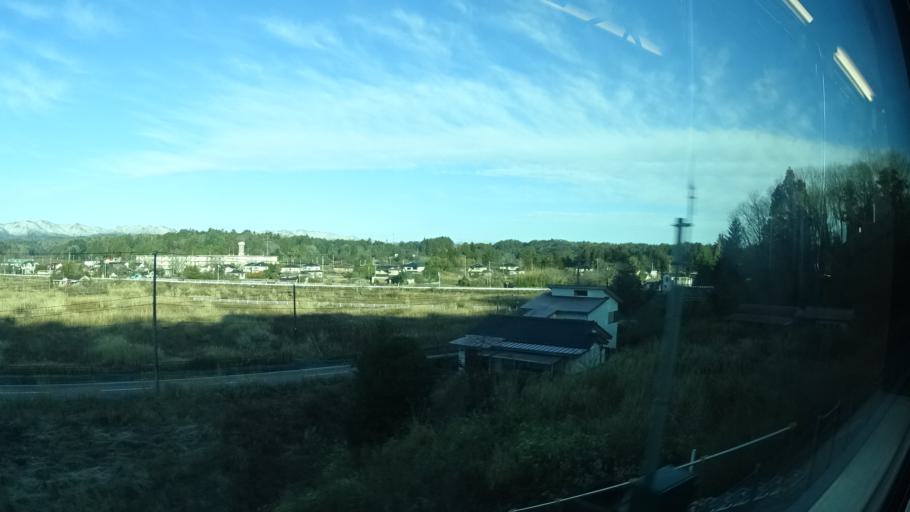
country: JP
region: Fukushima
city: Namie
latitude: 37.4374
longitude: 141.0010
